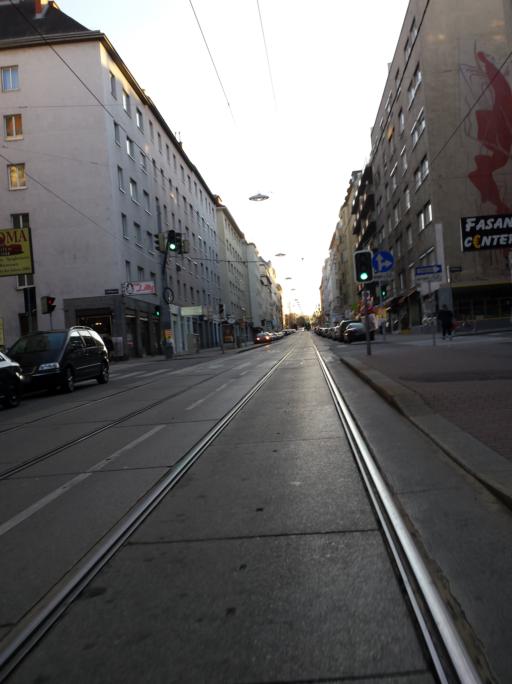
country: AT
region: Vienna
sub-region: Wien Stadt
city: Vienna
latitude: 48.1914
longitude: 16.3858
